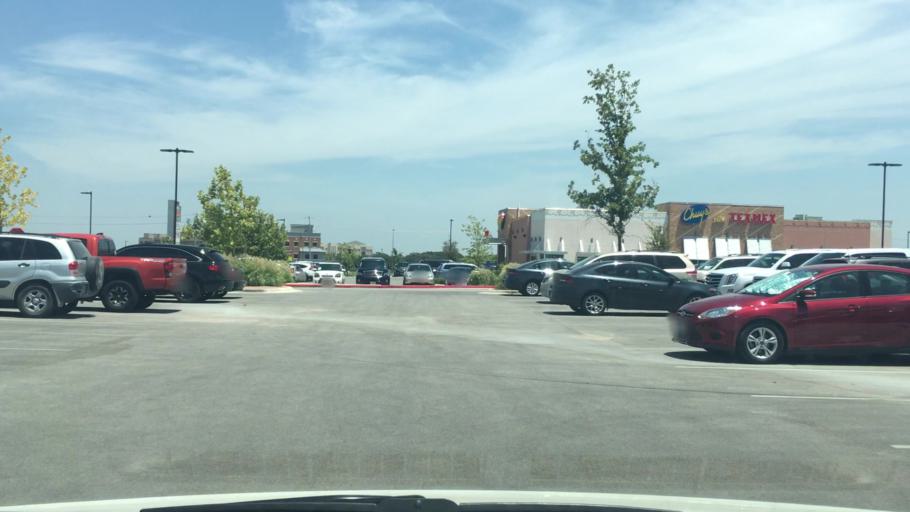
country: US
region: Texas
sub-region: Williamson County
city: Cedar Park
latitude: 30.5326
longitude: -97.8192
